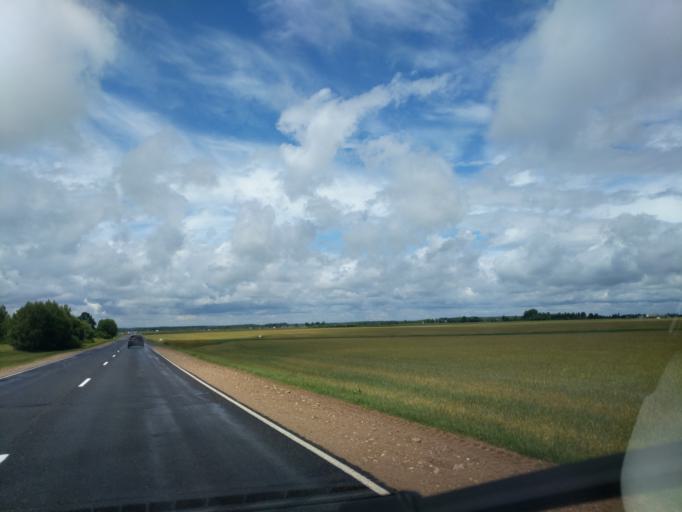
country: BY
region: Minsk
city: Il'ya
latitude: 54.3849
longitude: 27.3629
